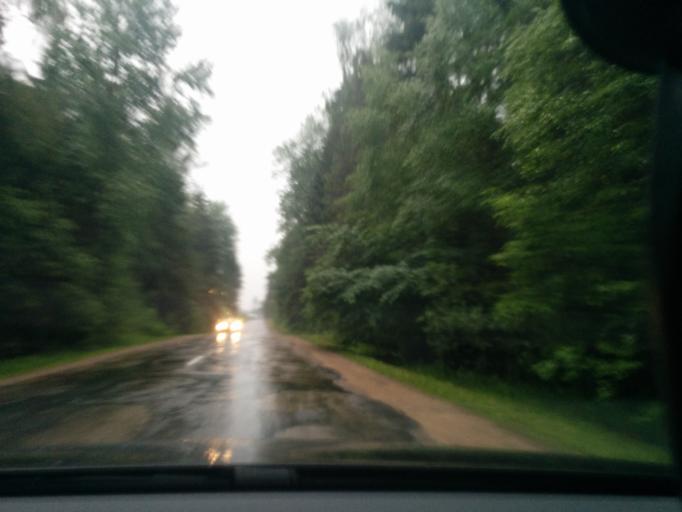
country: LV
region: Ogre
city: Ogre
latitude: 56.8325
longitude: 24.5857
